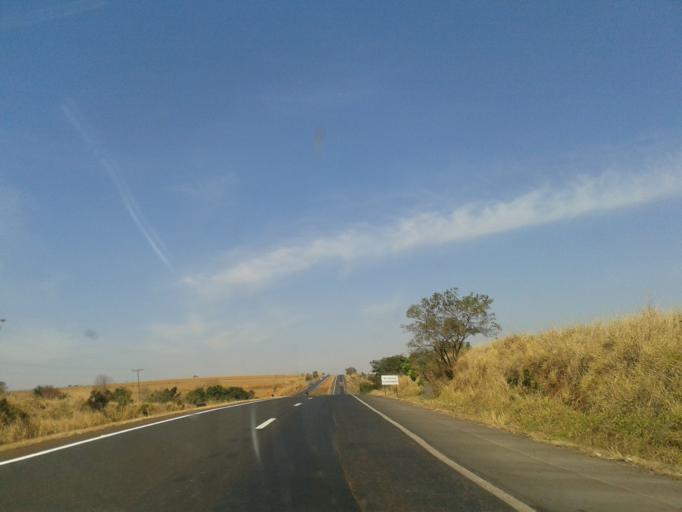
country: BR
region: Goias
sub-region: Goiatuba
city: Goiatuba
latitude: -18.1555
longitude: -49.2871
